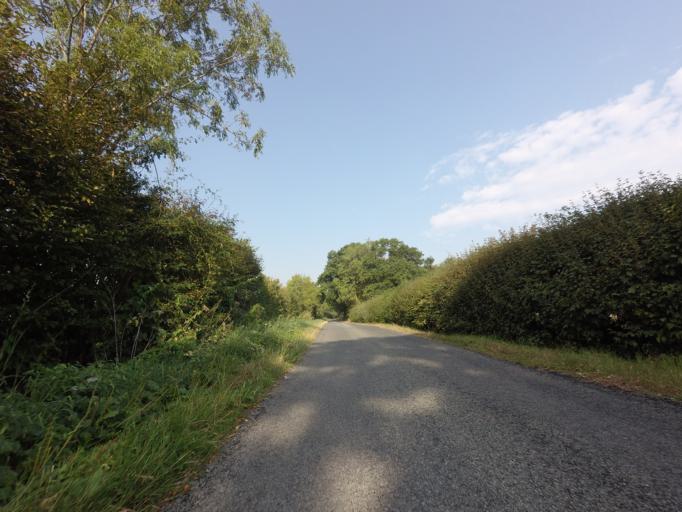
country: GB
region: England
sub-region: Kent
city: Headcorn
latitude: 51.1286
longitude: 0.6565
